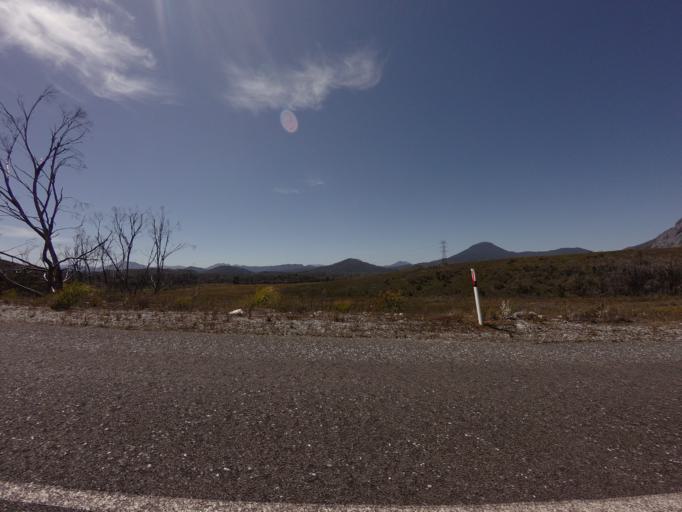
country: AU
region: Tasmania
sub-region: Huon Valley
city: Geeveston
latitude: -42.8539
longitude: 146.1880
